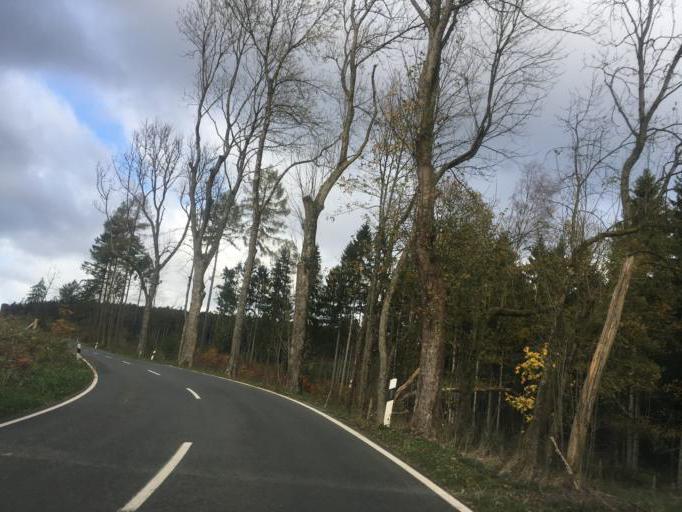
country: DE
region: Lower Saxony
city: Derental
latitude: 51.7545
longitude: 9.5057
